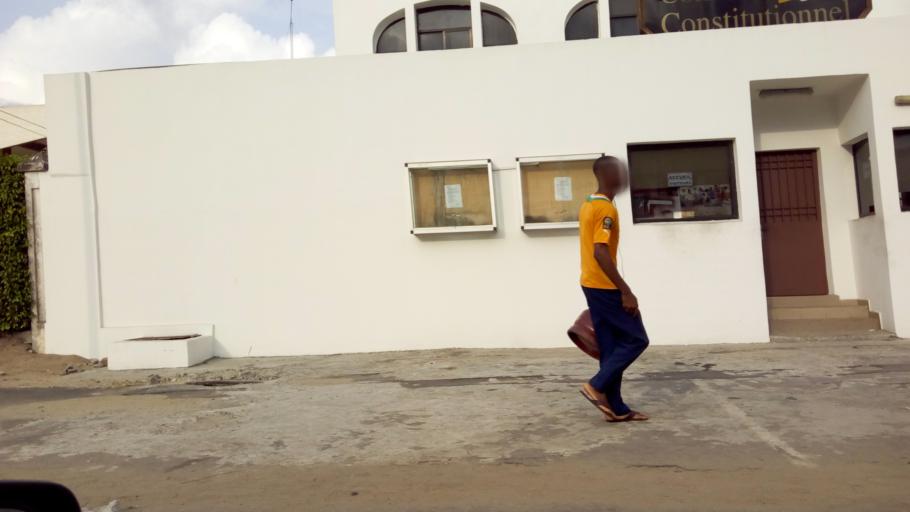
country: CI
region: Lagunes
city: Abidjan
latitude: 5.3289
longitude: -4.0239
